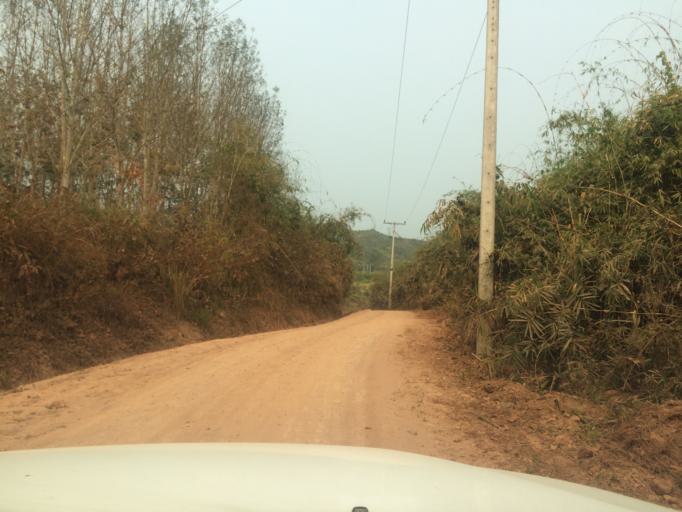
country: LA
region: Loungnamtha
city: Muang Nale
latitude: 20.4247
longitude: 101.7016
